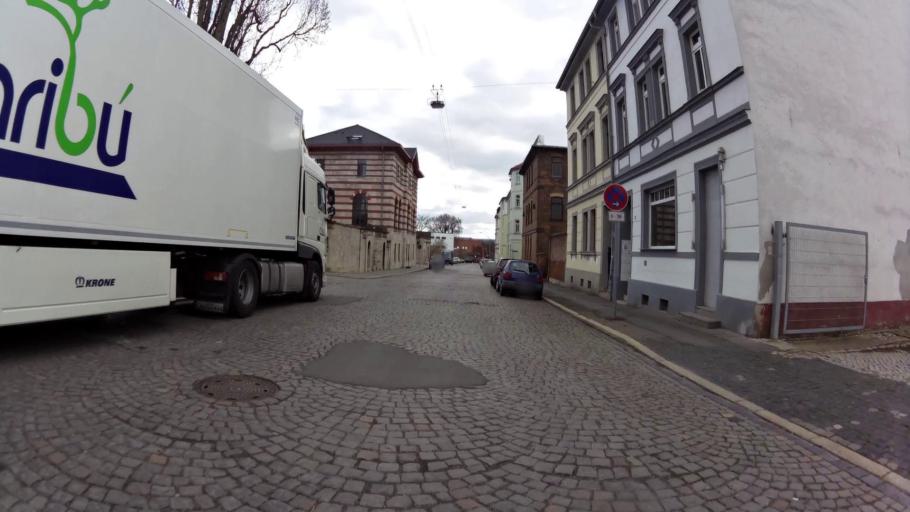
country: DE
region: Thuringia
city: Weimar
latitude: 50.9887
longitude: 11.3341
